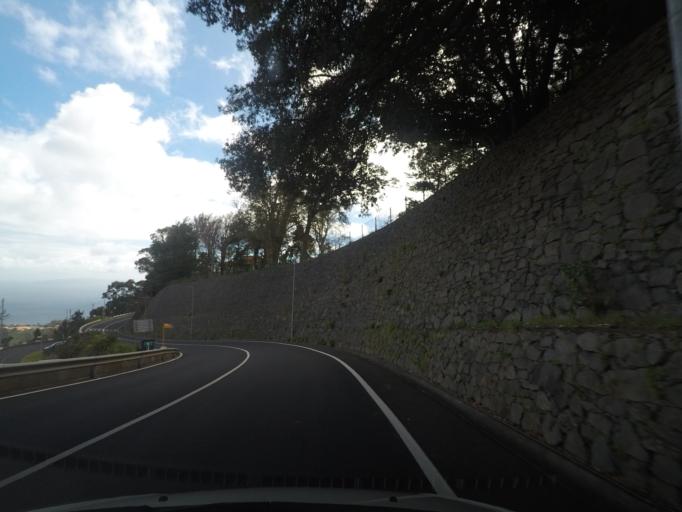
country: PT
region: Madeira
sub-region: Santa Cruz
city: Camacha
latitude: 32.6811
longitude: -16.8450
